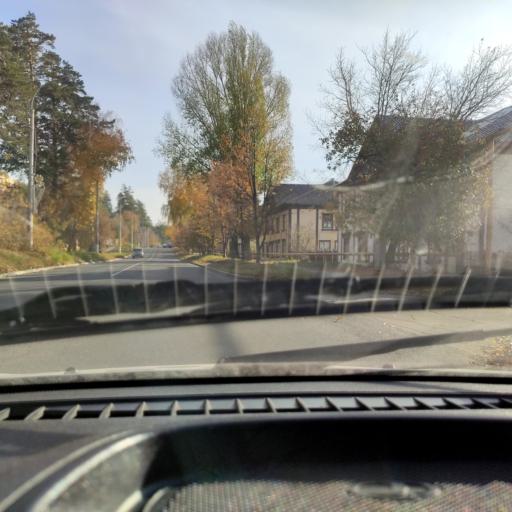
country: RU
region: Samara
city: Tol'yatti
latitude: 53.4760
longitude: 49.3709
